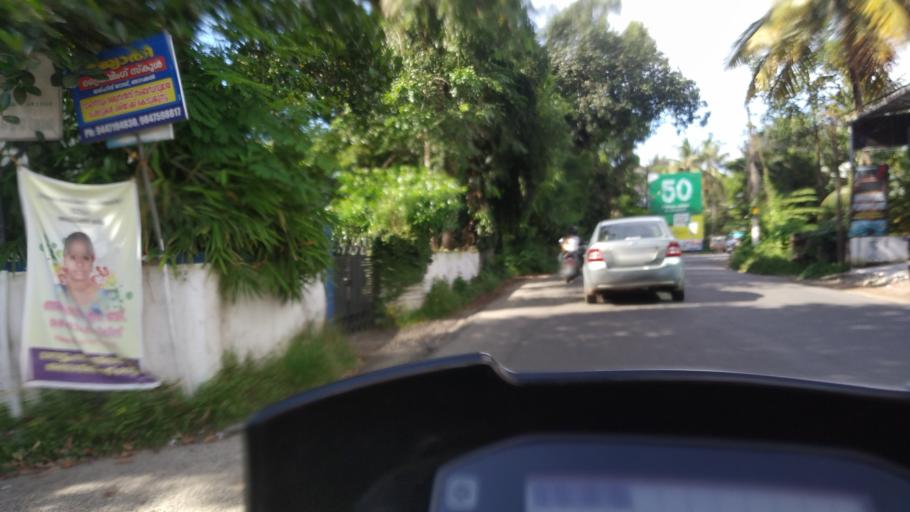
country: IN
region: Kerala
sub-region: Ernakulam
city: Elur
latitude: 10.0532
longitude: 76.2153
